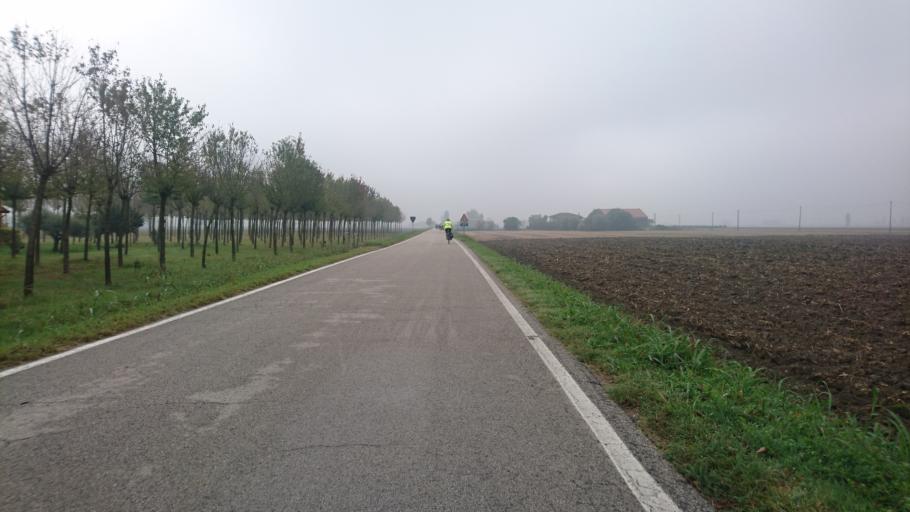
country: IT
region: Veneto
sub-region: Provincia di Padova
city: Pozzonovo
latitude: 45.1794
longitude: 11.7872
